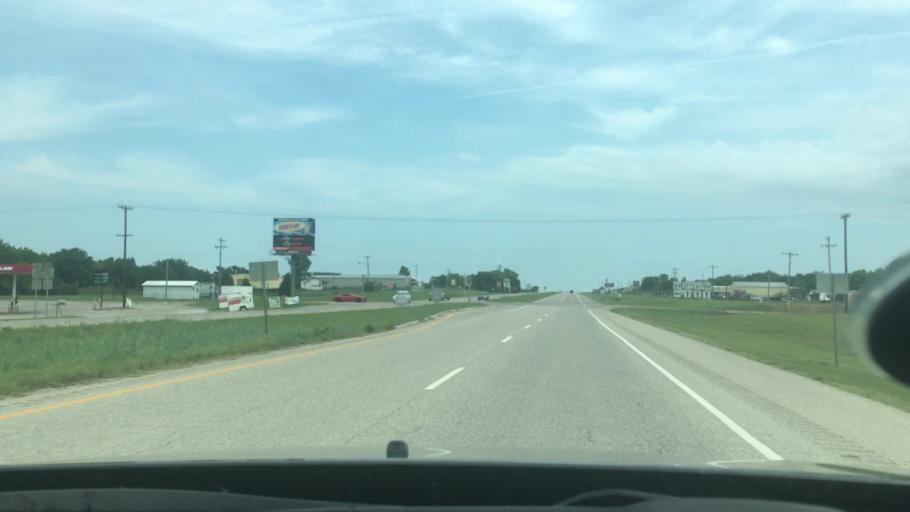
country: US
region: Oklahoma
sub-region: Seminole County
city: Seminole
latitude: 35.1872
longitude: -96.6750
